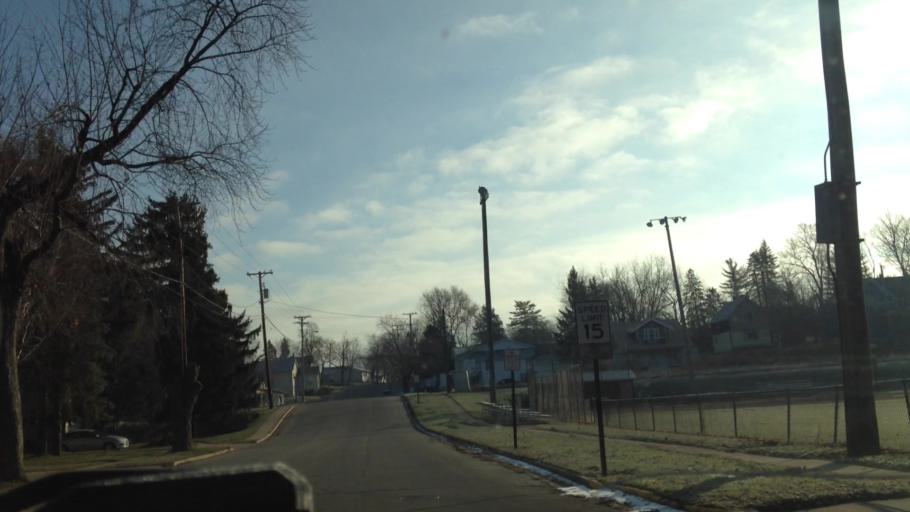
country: US
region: Wisconsin
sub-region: Dodge County
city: Mayville
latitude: 43.5012
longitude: -88.5485
